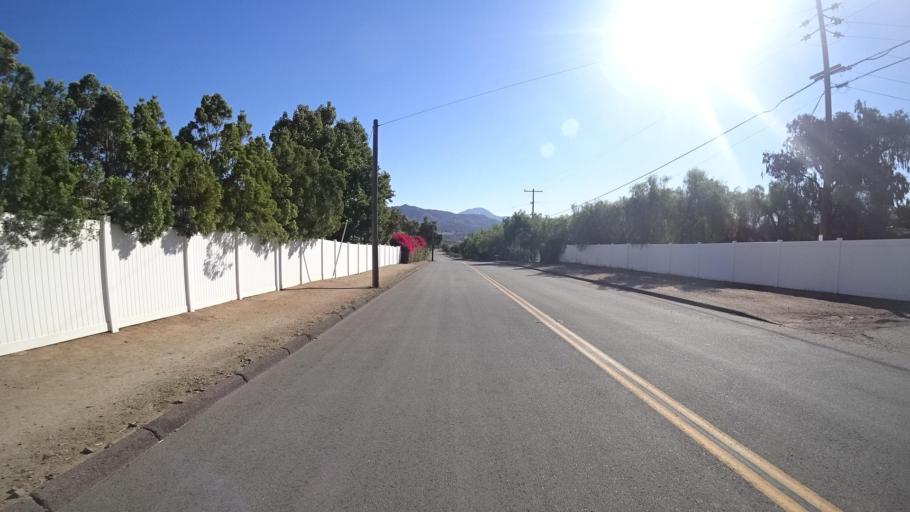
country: US
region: California
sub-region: San Diego County
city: Jamul
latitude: 32.7067
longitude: -116.8771
